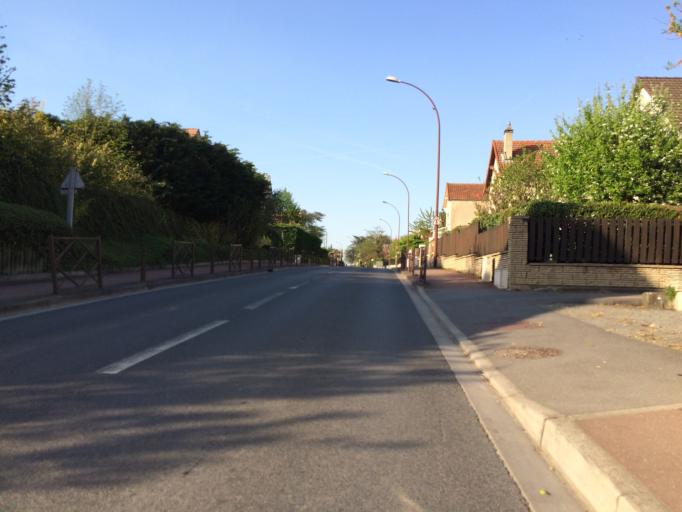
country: FR
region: Ile-de-France
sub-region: Departement des Hauts-de-Seine
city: Chatenay-Malabry
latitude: 48.7570
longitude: 2.2765
